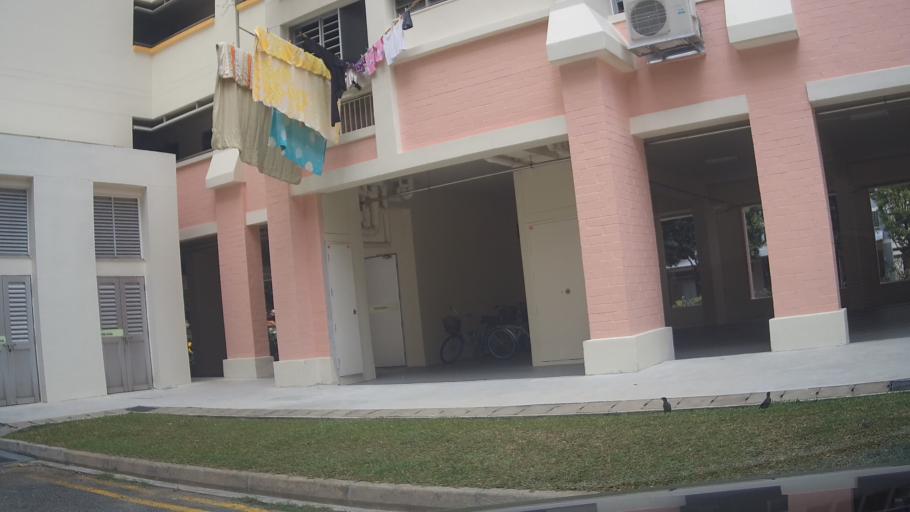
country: MY
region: Johor
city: Johor Bahru
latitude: 1.4401
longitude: 103.7929
